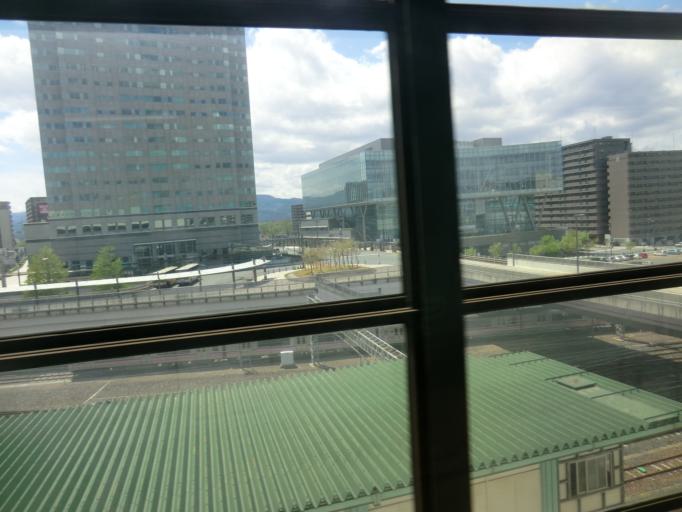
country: JP
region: Iwate
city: Morioka-shi
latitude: 39.7010
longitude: 141.1370
